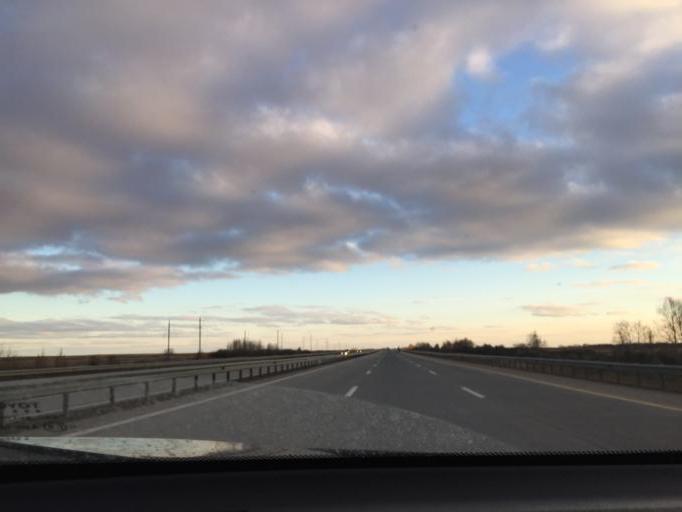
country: KZ
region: Astana Qalasy
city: Astana
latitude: 51.3479
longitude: 71.3376
